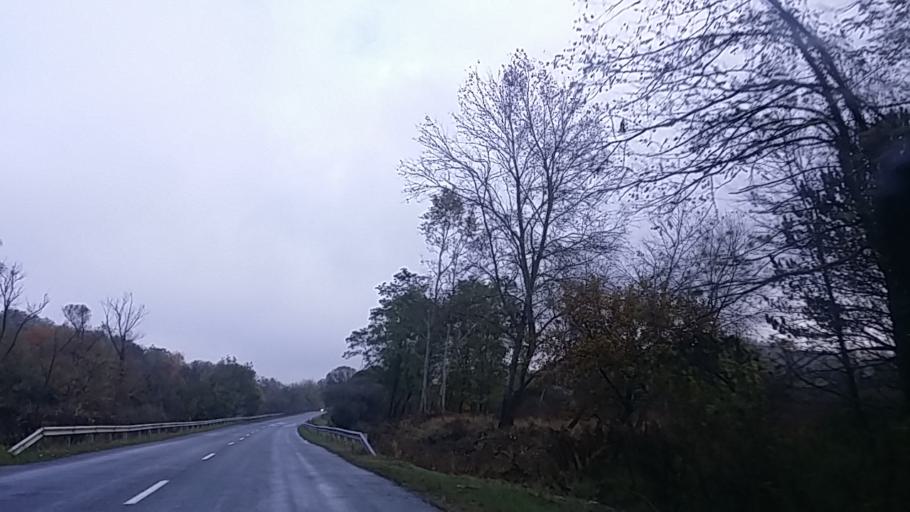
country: HU
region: Heves
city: Belapatfalva
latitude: 48.0735
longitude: 20.3586
